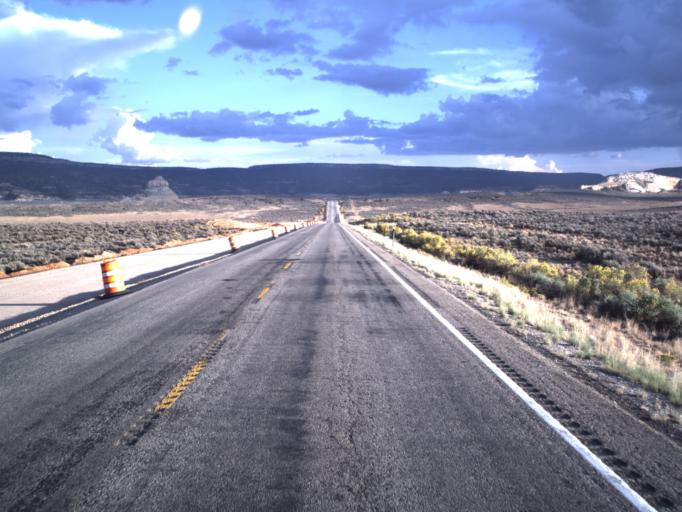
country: US
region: Utah
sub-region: San Juan County
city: Monticello
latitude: 38.0917
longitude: -109.3572
